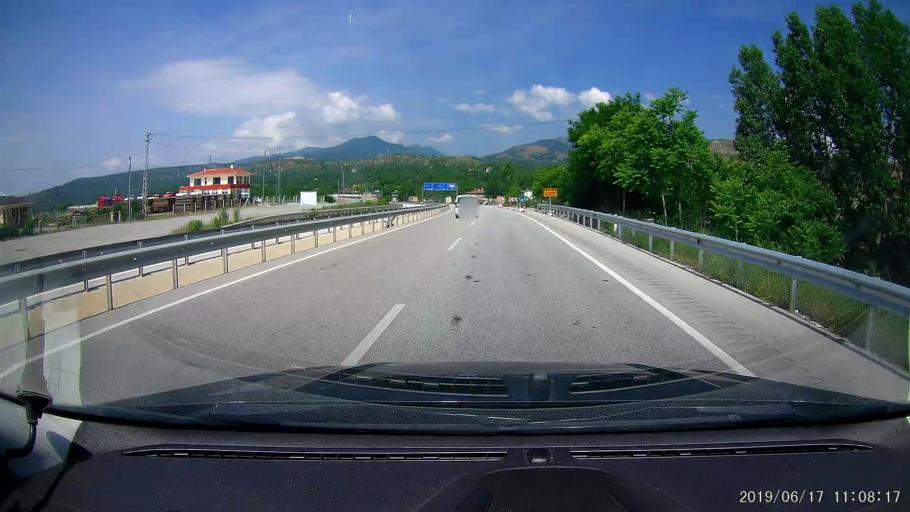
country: TR
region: Kastamonu
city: Tosya
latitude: 41.0009
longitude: 34.0393
